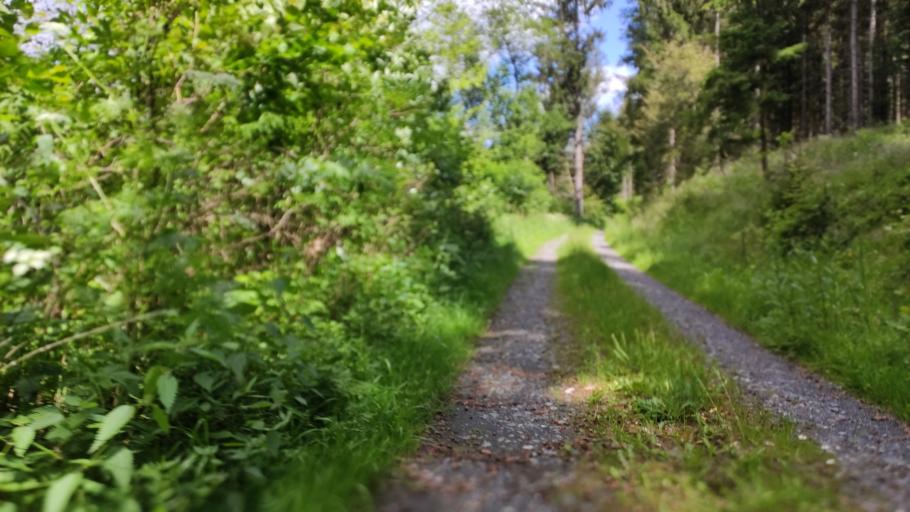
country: DE
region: Bavaria
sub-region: Upper Franconia
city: Tschirn
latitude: 50.4184
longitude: 11.4715
